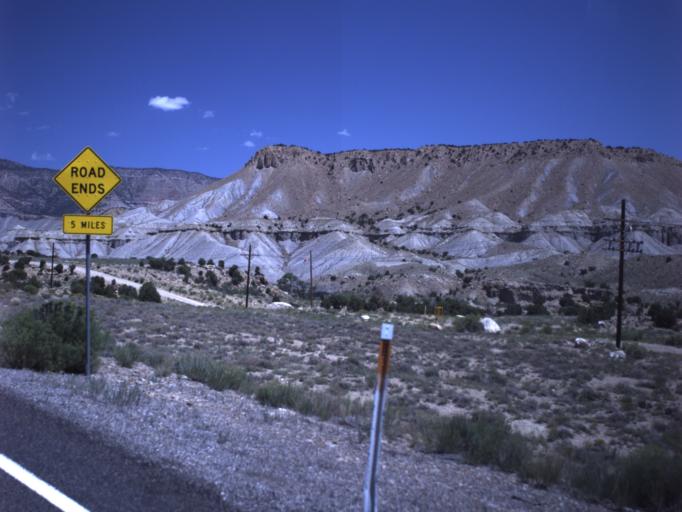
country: US
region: Utah
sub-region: Emery County
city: Orangeville
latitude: 39.2619
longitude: -111.0987
